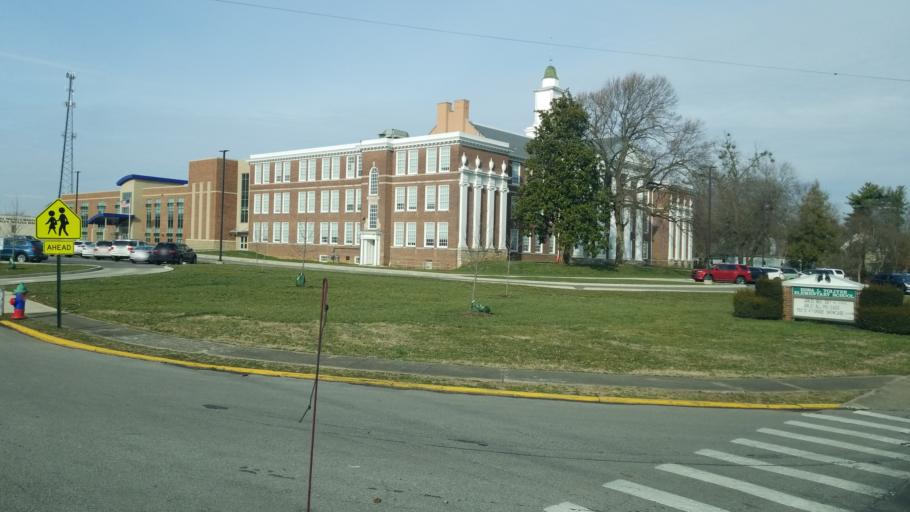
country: US
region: Kentucky
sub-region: Boyle County
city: Danville
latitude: 37.6471
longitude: -84.7824
